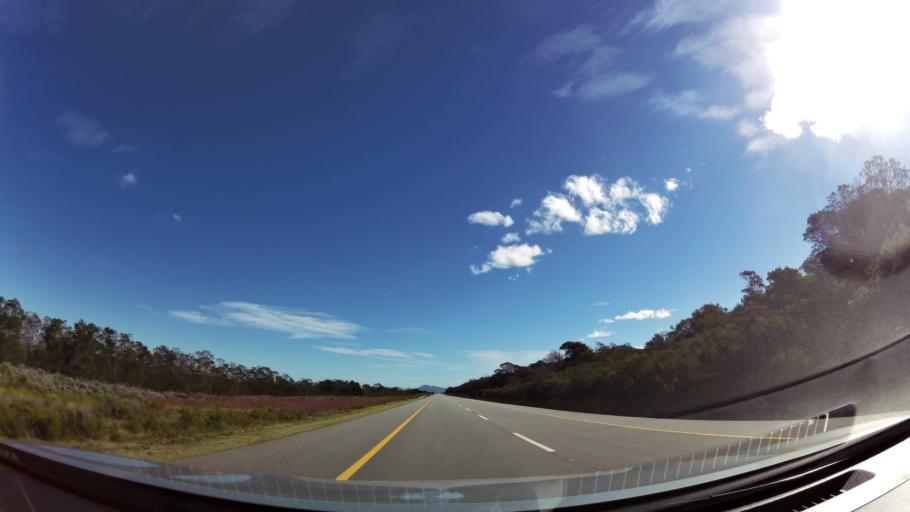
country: ZA
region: Eastern Cape
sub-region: Cacadu District Municipality
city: Kruisfontein
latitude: -33.9947
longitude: 24.7229
